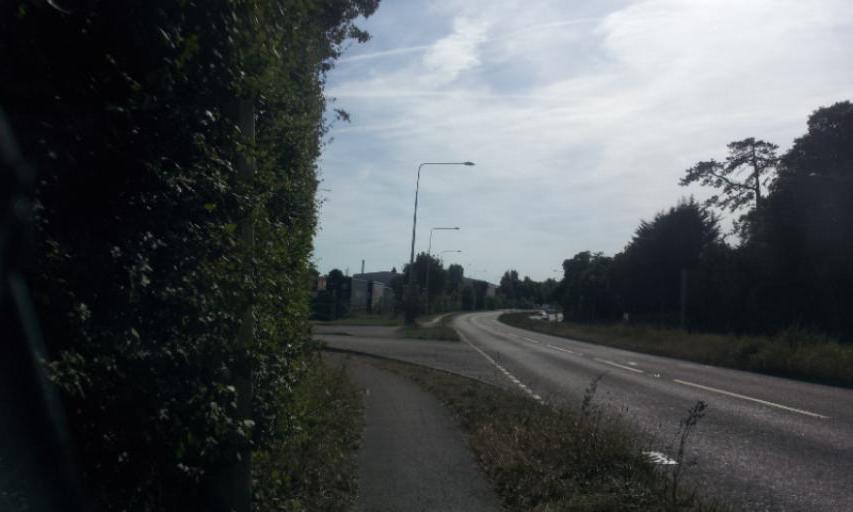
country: GB
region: England
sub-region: Medway
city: Halling
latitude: 51.3406
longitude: 0.4458
